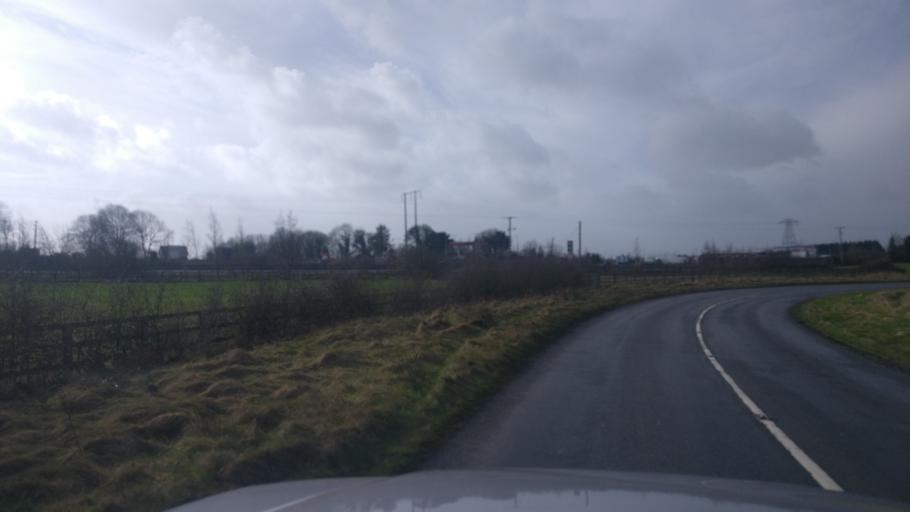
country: IE
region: Connaught
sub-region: County Galway
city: Loughrea
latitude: 53.2667
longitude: -8.6016
